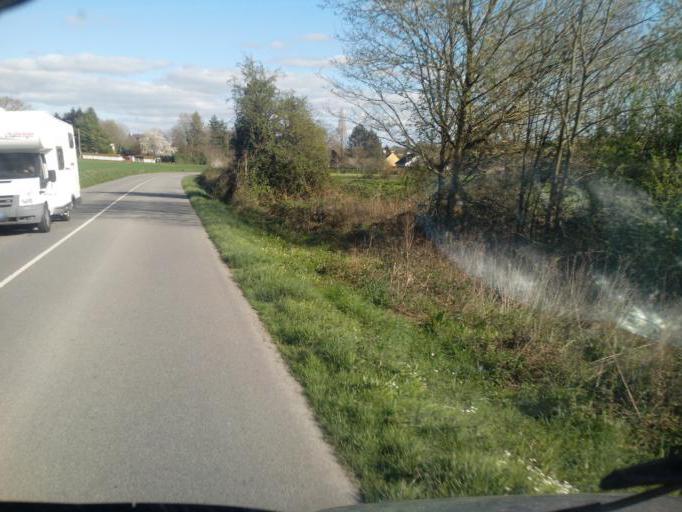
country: FR
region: Brittany
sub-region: Departement d'Ille-et-Vilaine
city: Guipry
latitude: 47.8424
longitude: -1.8606
